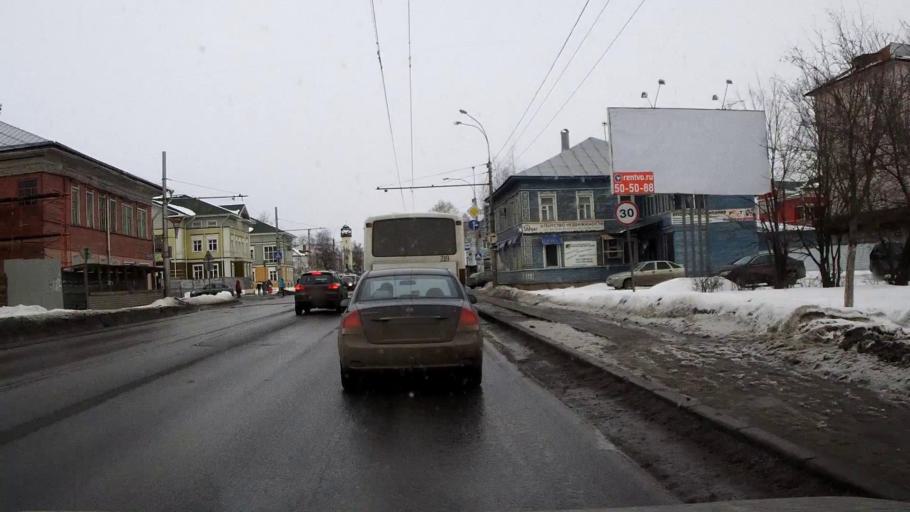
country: RU
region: Vologda
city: Vologda
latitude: 59.2263
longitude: 39.8937
